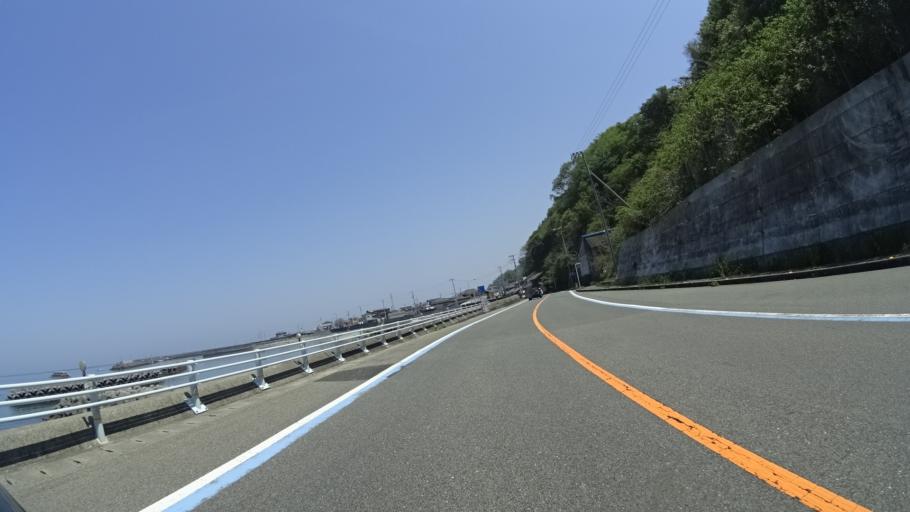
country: JP
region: Ehime
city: Ozu
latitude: 33.6061
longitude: 132.4736
